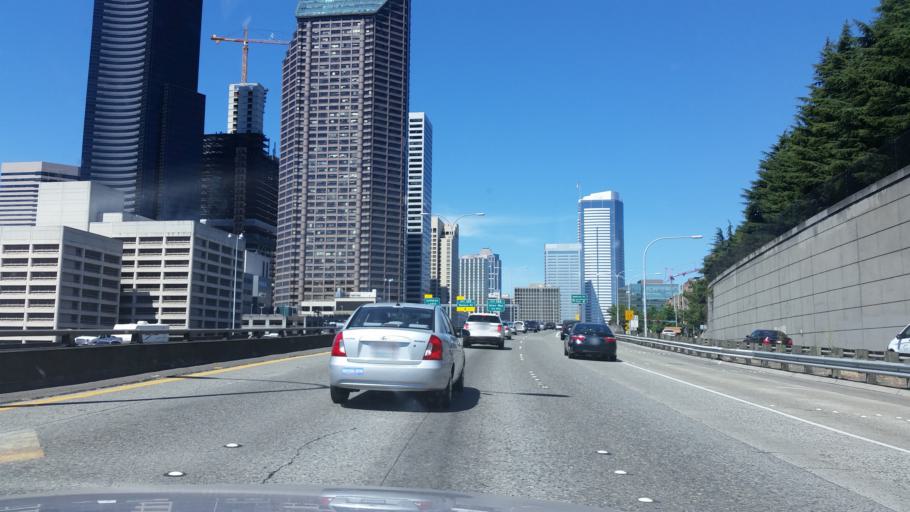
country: US
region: Washington
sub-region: King County
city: Seattle
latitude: 47.6028
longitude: -122.3257
